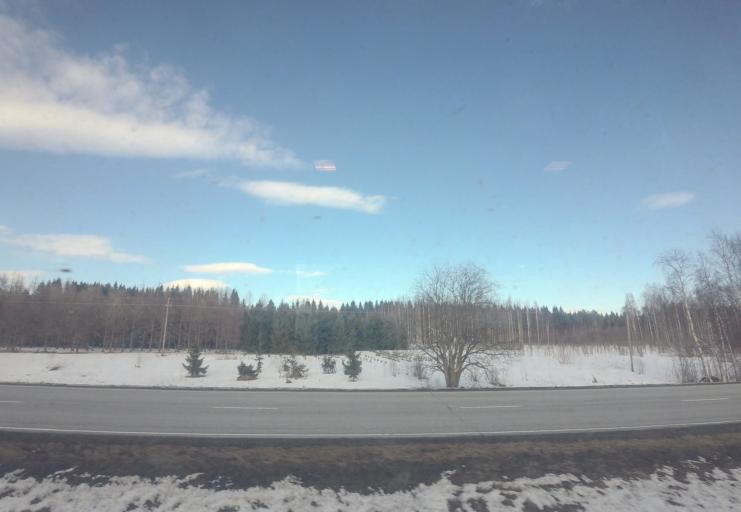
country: FI
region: Southern Savonia
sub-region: Savonlinna
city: Punkaharju
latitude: 61.7910
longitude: 29.3421
